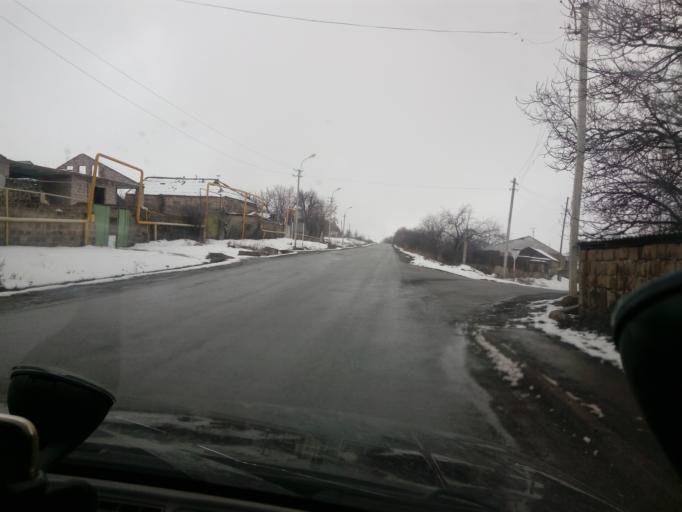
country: AM
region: Kotayk'i Marz
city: Hrazdan
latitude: 40.4752
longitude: 44.7412
